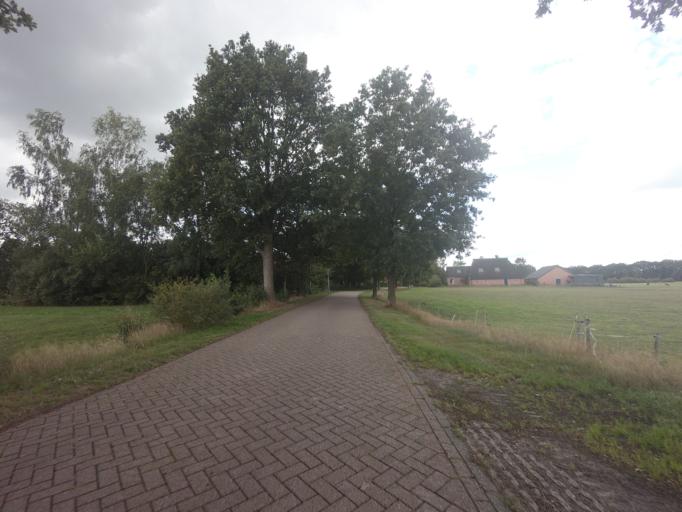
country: NL
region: Drenthe
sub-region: Gemeente Westerveld
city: Dwingeloo
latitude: 52.9638
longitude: 6.2842
